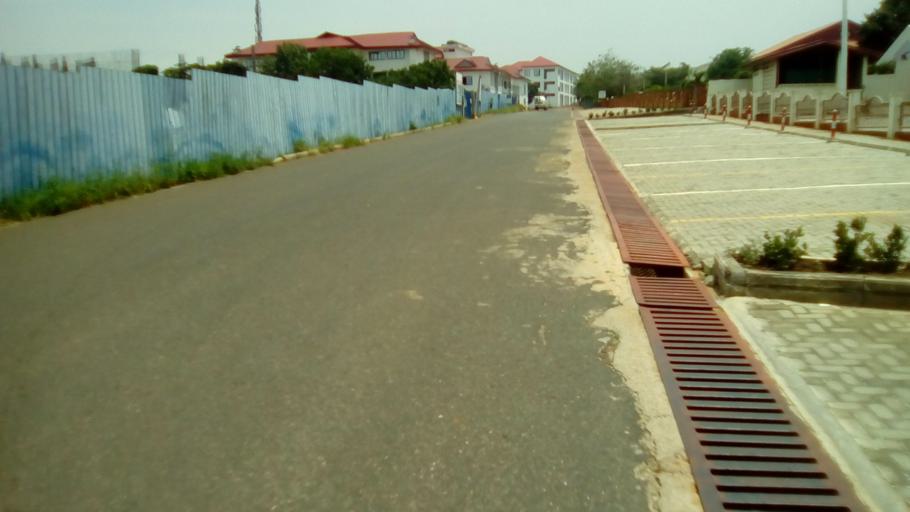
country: GH
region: Greater Accra
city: Medina Estates
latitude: 5.6563
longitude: -0.1900
